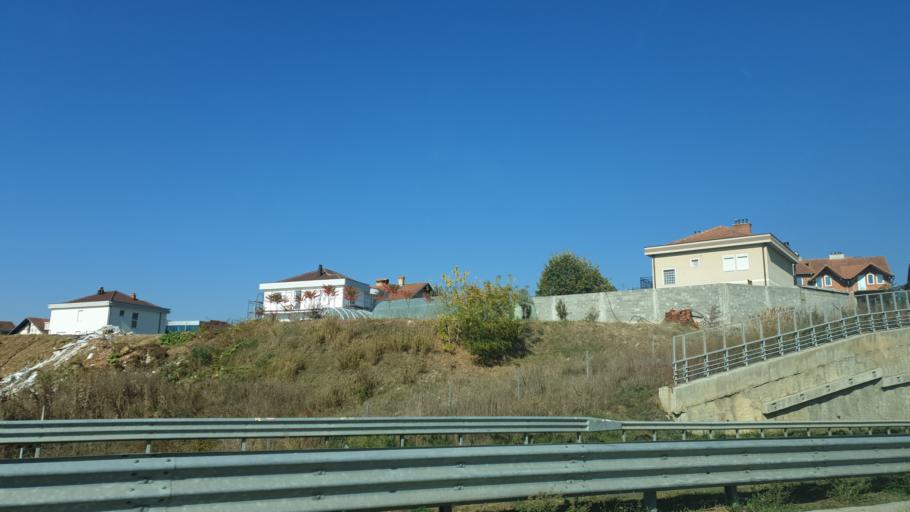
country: XK
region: Prizren
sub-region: Komuna e Therandes
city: Suva Reka
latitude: 42.3571
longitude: 20.8063
